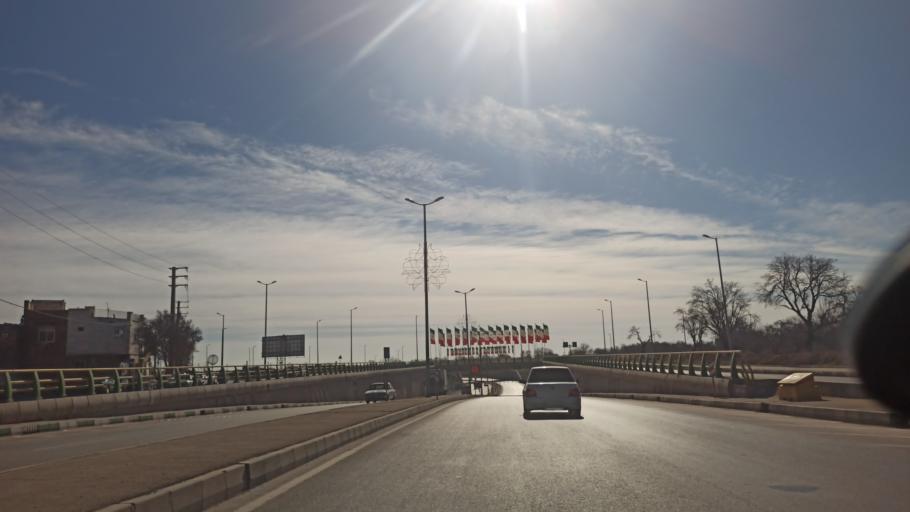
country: IR
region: Qazvin
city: Qazvin
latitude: 36.2469
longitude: 50.0017
